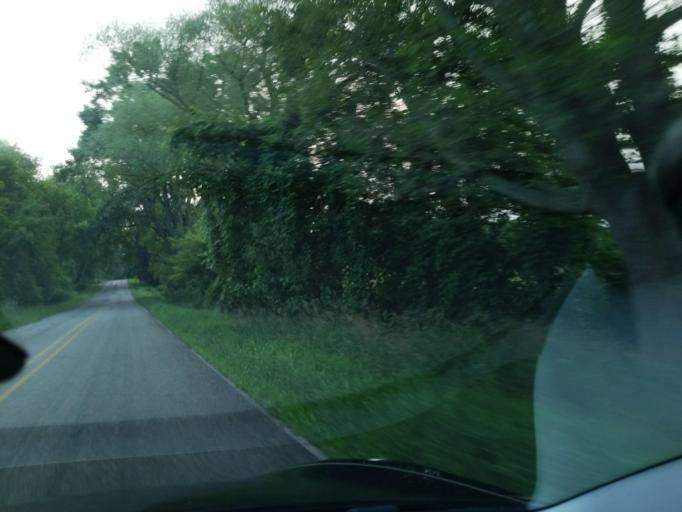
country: US
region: Michigan
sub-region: Ingham County
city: Leslie
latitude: 42.3495
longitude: -84.4780
